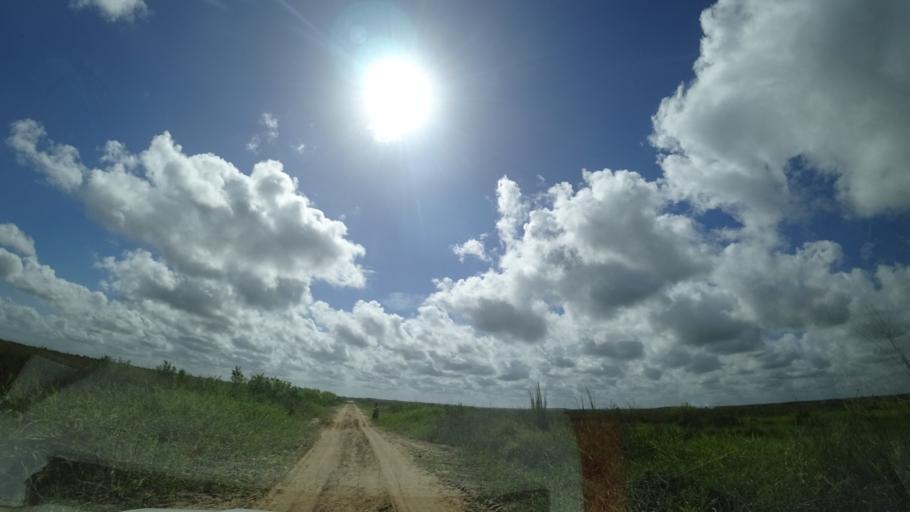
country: MZ
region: Sofala
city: Dondo
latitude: -19.3986
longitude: 34.5700
